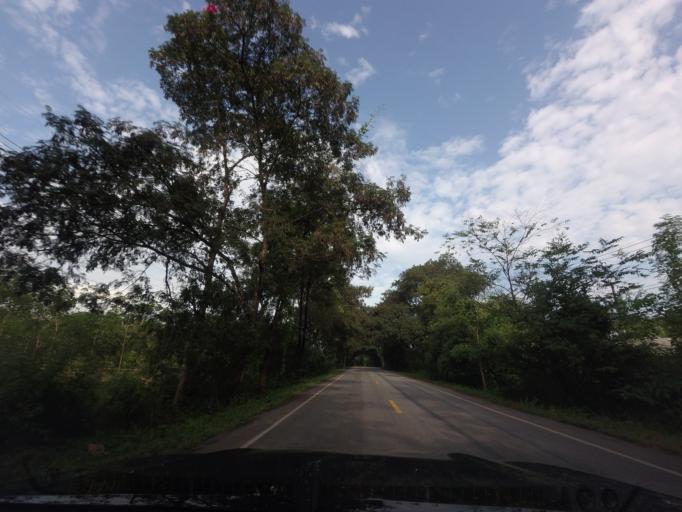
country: TH
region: Nong Khai
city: Pho Tak
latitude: 17.7886
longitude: 102.3633
